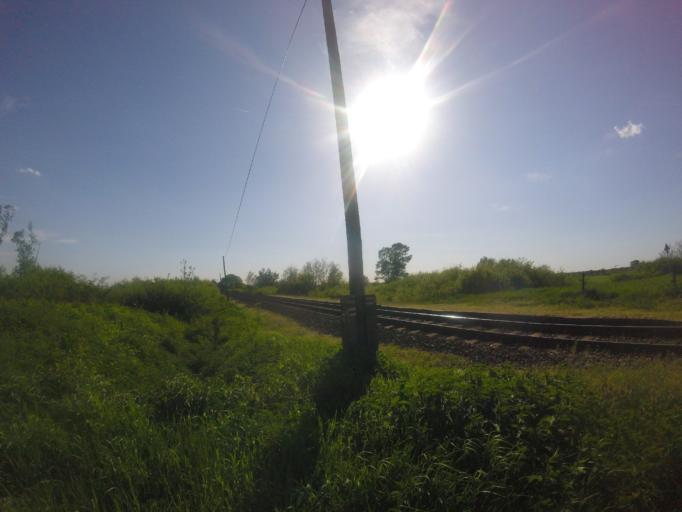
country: HU
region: Bekes
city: Gyula
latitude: 46.6946
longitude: 21.3227
